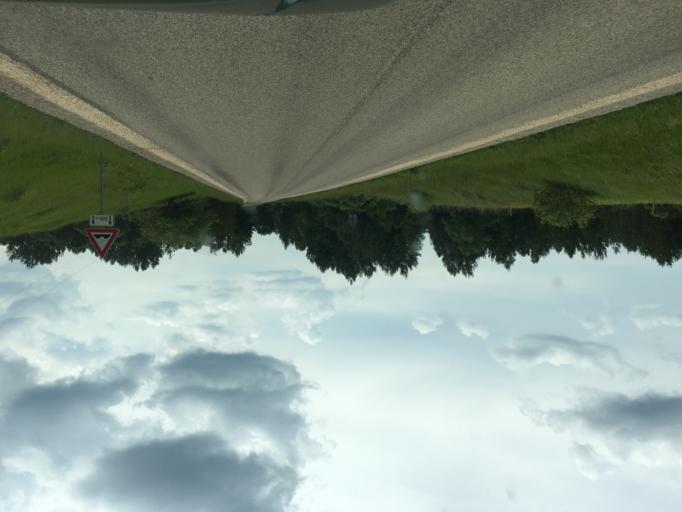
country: LV
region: Rugaju
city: Rugaji
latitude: 56.8464
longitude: 27.0915
